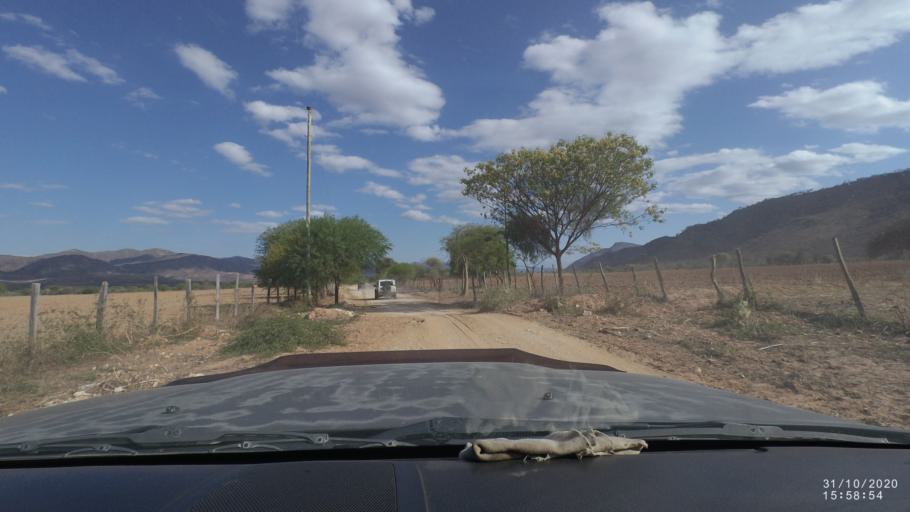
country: BO
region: Chuquisaca
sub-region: Provincia Zudanez
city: Mojocoya
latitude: -18.3271
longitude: -64.6707
